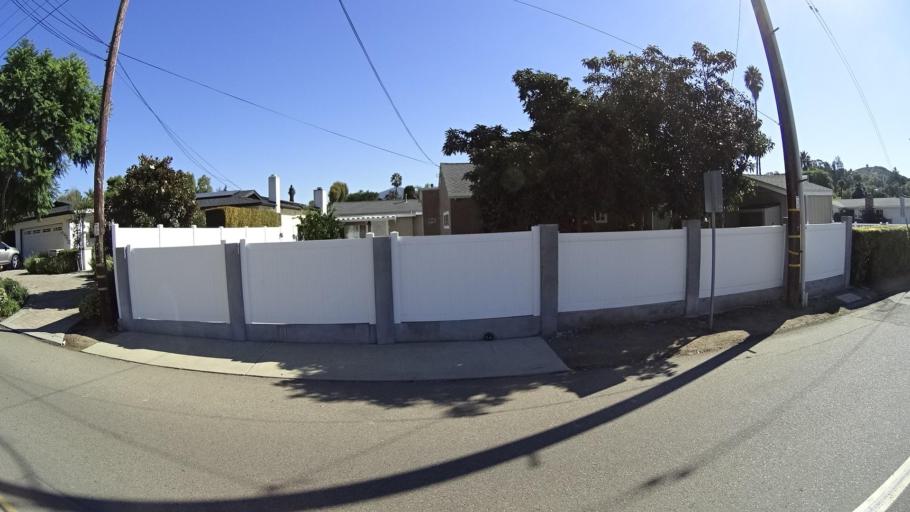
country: US
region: California
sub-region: San Diego County
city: Bonita
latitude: 32.6702
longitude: -117.0190
